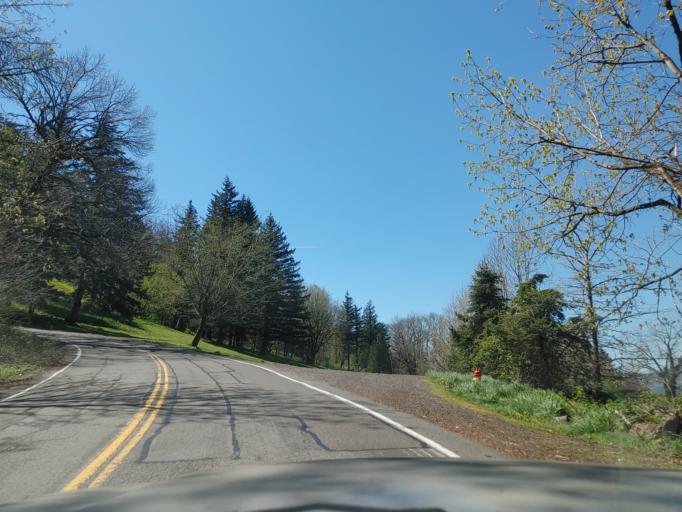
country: US
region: Washington
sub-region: Clark County
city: Washougal
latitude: 45.5405
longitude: -122.2875
